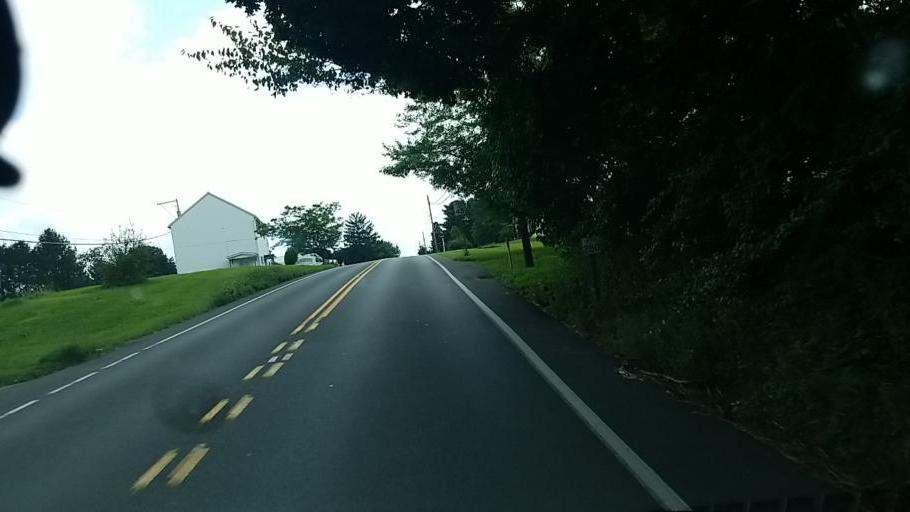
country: US
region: Pennsylvania
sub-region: Dauphin County
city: Elizabethville
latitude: 40.5148
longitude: -76.8616
